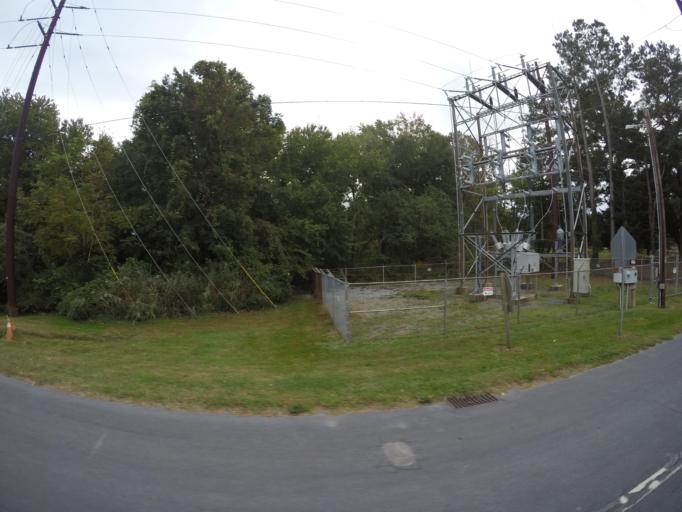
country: US
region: Delaware
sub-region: Sussex County
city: Lewes
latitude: 38.7581
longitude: -75.1564
